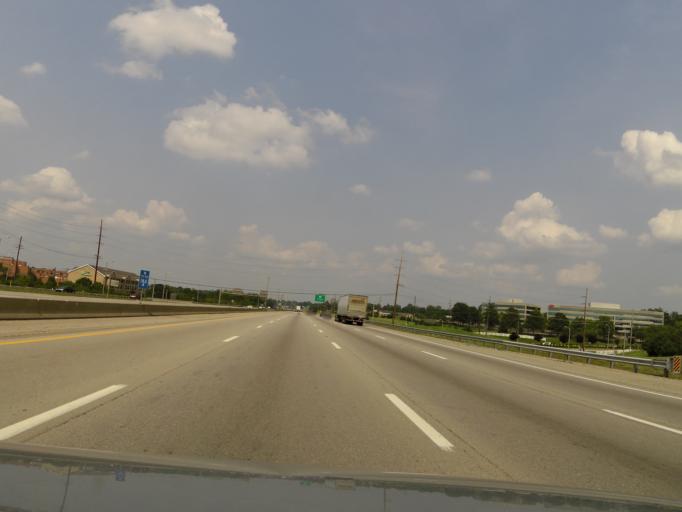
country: US
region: Kentucky
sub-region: Boone County
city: Florence
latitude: 39.0120
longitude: -84.6322
